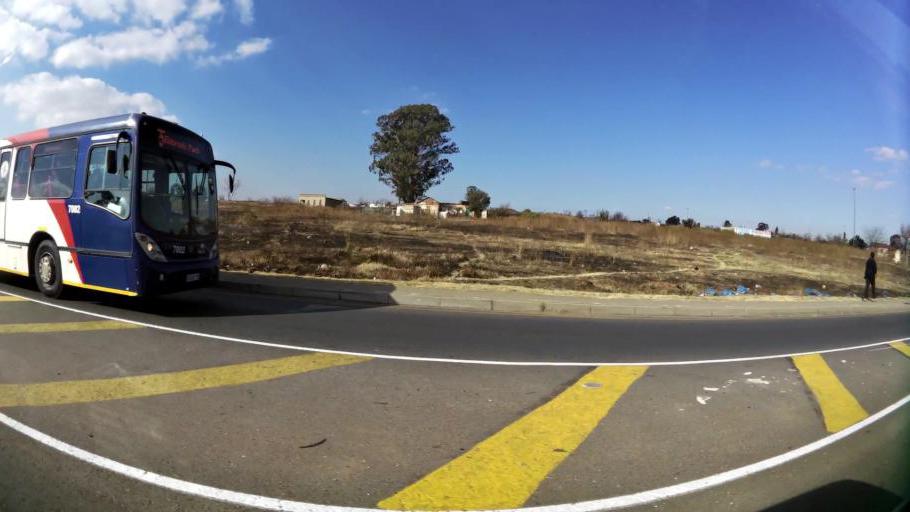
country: ZA
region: Gauteng
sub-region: City of Johannesburg Metropolitan Municipality
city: Soweto
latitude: -26.2642
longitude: 27.8897
